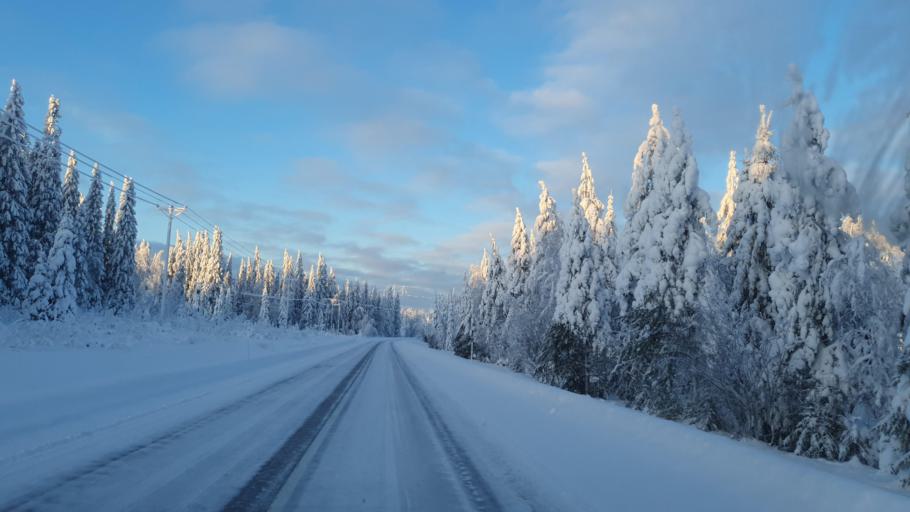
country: FI
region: Kainuu
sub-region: Kajaani
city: Vuokatti
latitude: 64.2323
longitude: 28.2391
